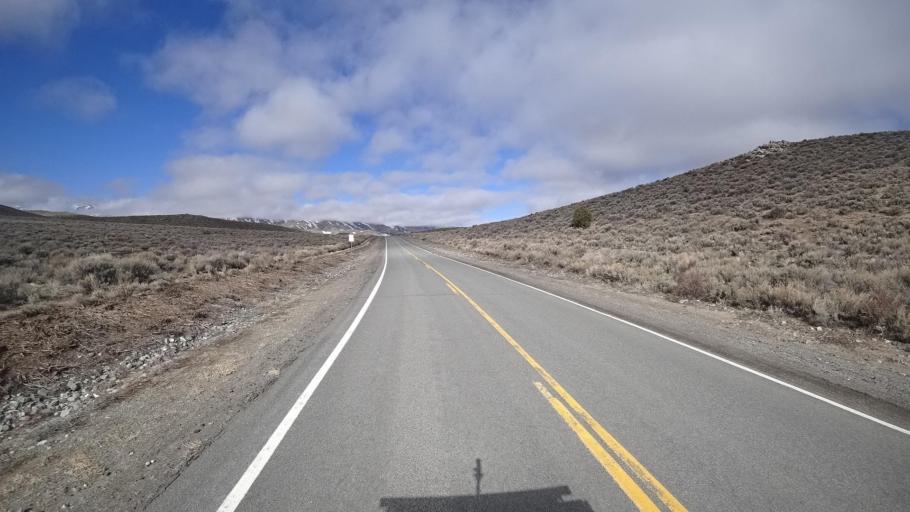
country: US
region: Nevada
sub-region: Washoe County
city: Cold Springs
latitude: 39.8008
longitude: -119.9049
